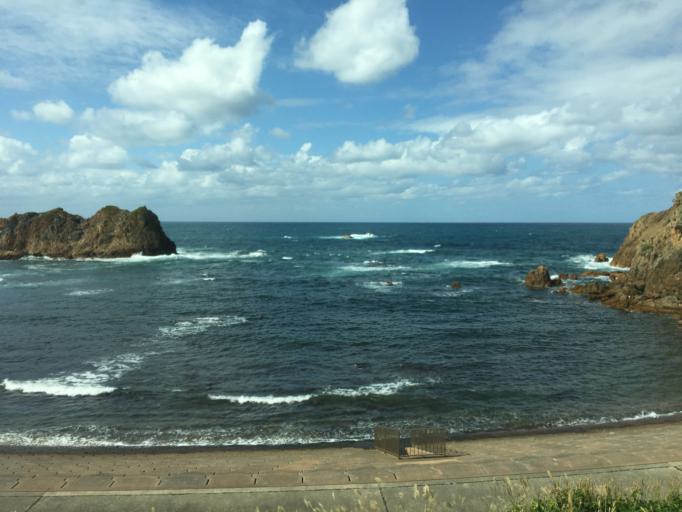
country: JP
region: Aomori
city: Shimokizukuri
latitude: 40.6600
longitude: 139.9380
